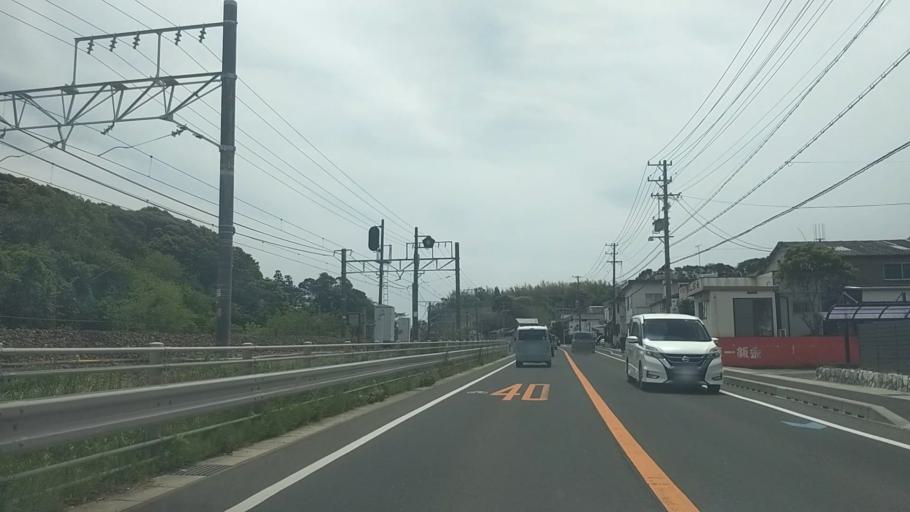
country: JP
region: Shizuoka
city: Kosai-shi
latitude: 34.7003
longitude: 137.5558
